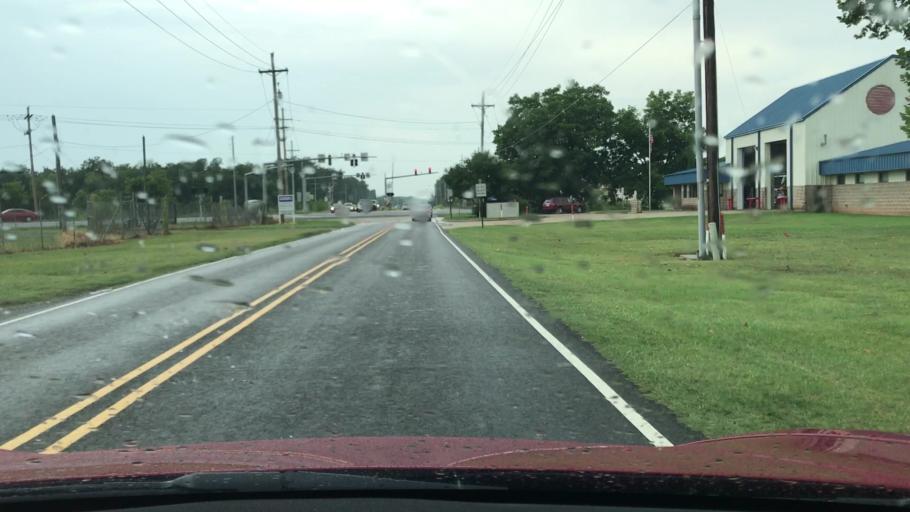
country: US
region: Louisiana
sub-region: Bossier Parish
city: Bossier City
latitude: 32.4009
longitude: -93.6921
